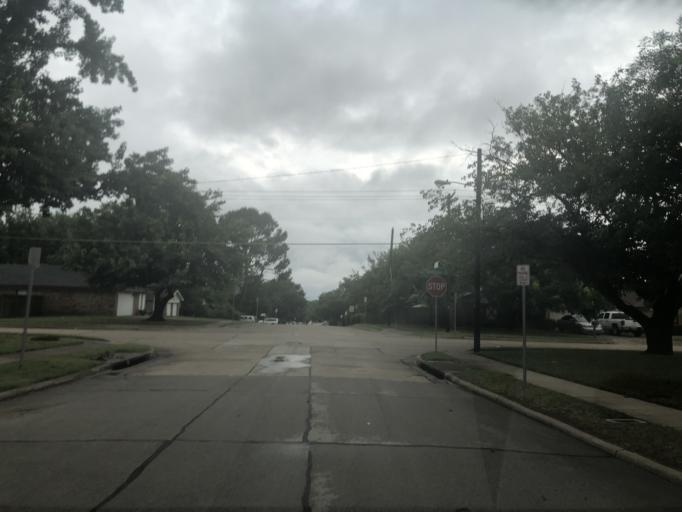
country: US
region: Texas
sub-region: Dallas County
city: Irving
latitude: 32.7943
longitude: -96.9507
